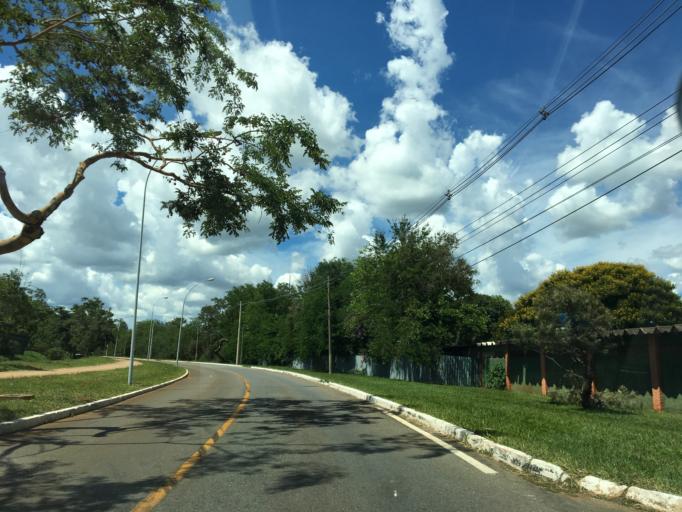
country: BR
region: Federal District
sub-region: Brasilia
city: Brasilia
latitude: -15.8140
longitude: -47.8359
